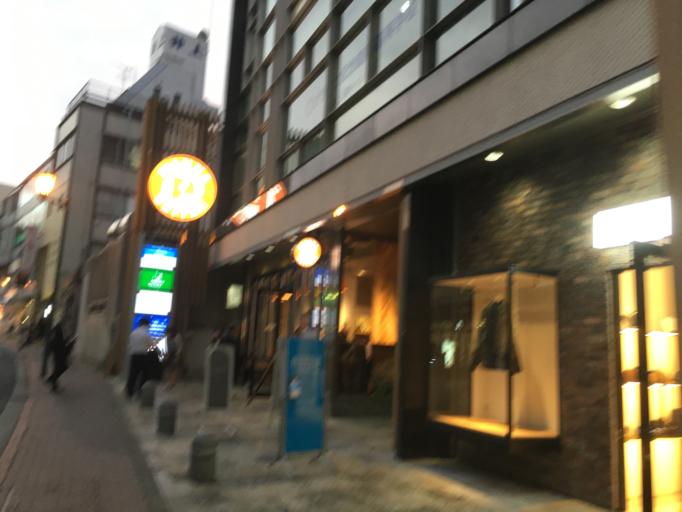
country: JP
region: Kumamoto
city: Kumamoto
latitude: 32.8037
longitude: 130.7098
